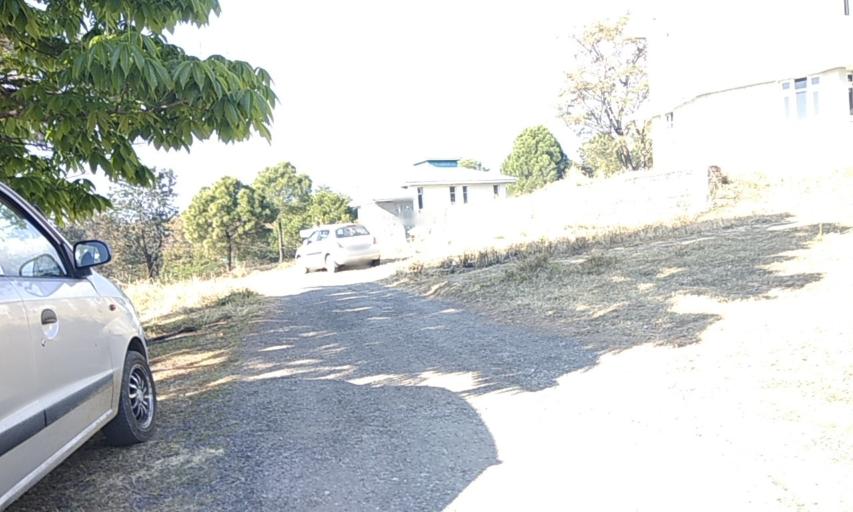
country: IN
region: Himachal Pradesh
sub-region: Kangra
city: Palampur
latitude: 32.1024
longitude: 76.5486
